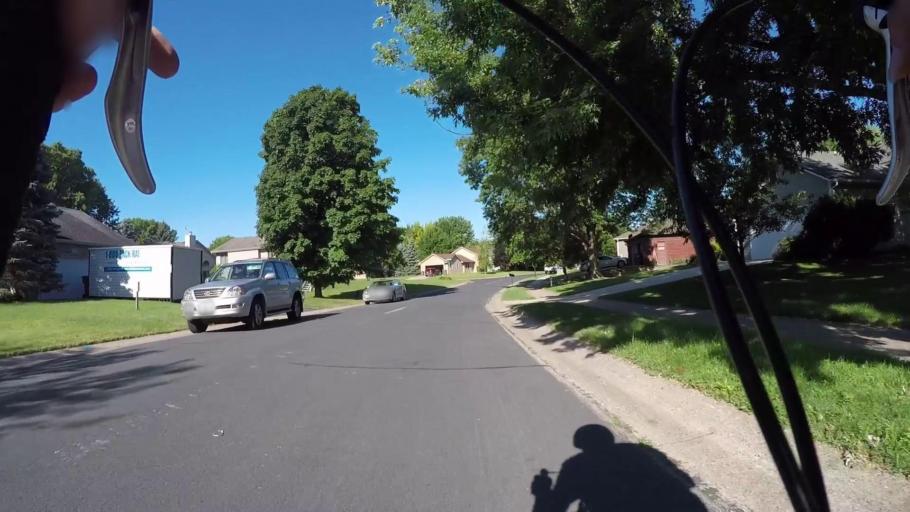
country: US
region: Minnesota
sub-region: Carver County
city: Chanhassen
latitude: 44.8743
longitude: -93.5018
